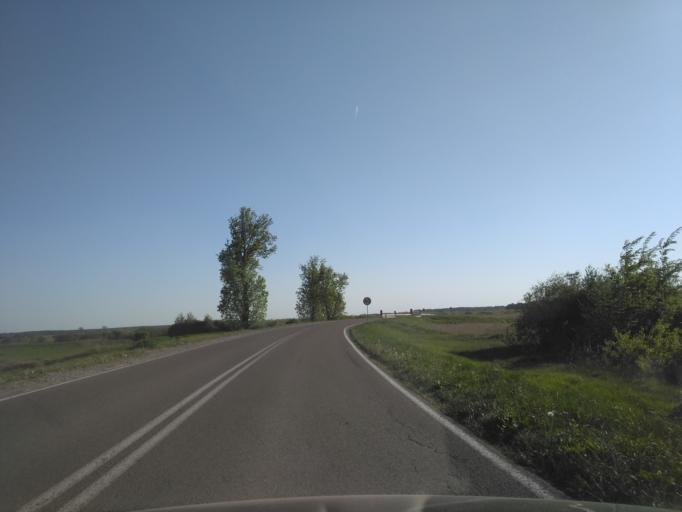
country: PL
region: Lublin Voivodeship
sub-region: Powiat swidnicki
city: Trawniki
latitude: 51.1783
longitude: 23.0506
